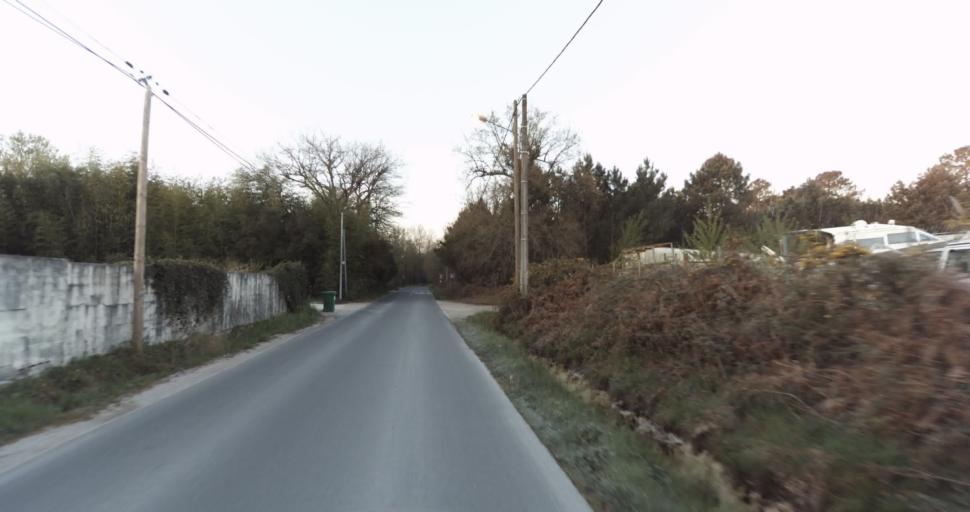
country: FR
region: Aquitaine
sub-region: Departement de la Gironde
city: Saint-Aubin-de-Medoc
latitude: 44.8069
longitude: -0.7276
